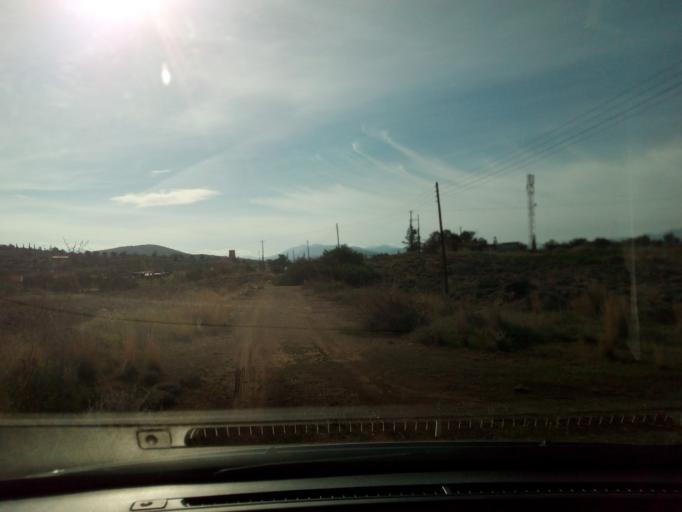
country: CY
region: Lefkosia
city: Klirou
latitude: 35.0431
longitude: 33.1440
